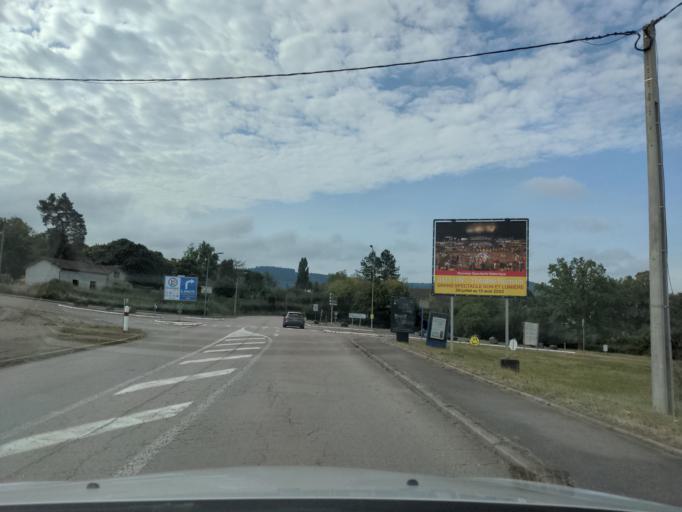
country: FR
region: Bourgogne
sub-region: Departement de Saone-et-Loire
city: Autun
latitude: 46.9681
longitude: 4.3052
